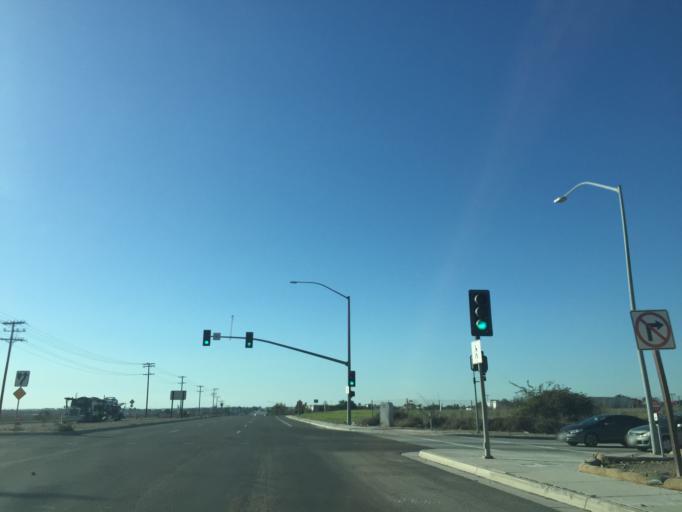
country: MX
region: Baja California
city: Tijuana
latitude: 32.5678
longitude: -116.9495
